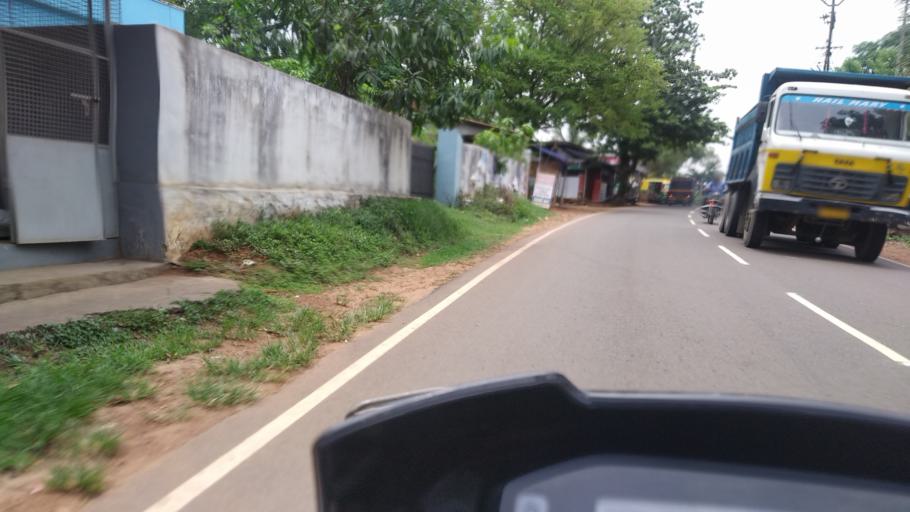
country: IN
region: Kerala
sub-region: Ernakulam
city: Aluva
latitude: 10.1565
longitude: 76.3239
